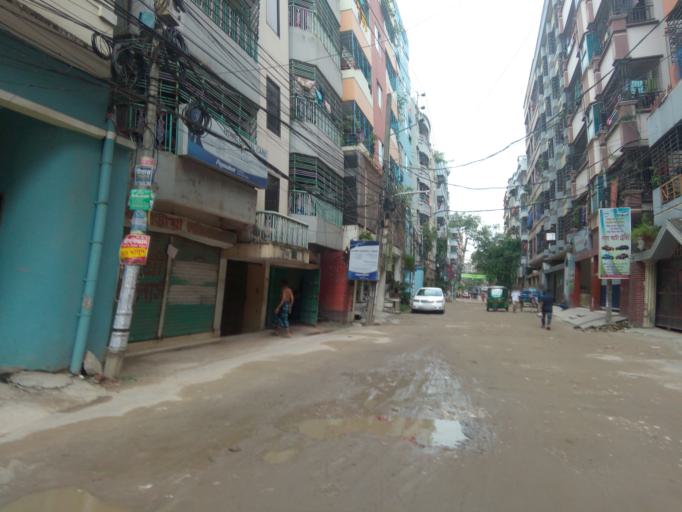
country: BD
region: Dhaka
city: Paltan
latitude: 23.7637
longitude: 90.4264
